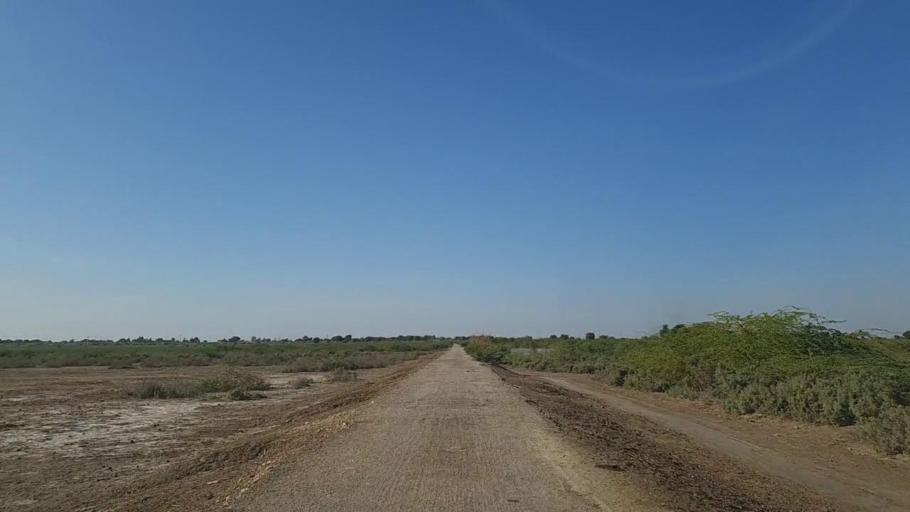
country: PK
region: Sindh
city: Samaro
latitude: 25.2550
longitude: 69.4913
